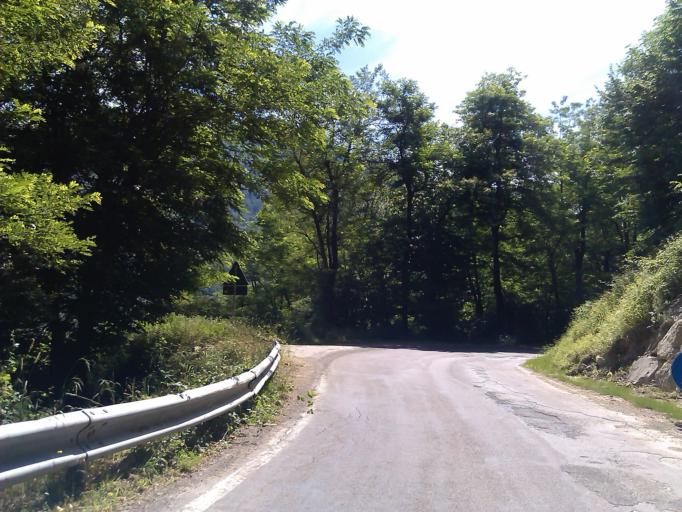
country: IT
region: Tuscany
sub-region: Provincia di Pistoia
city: Sambuca Pistoiese
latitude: 44.1027
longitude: 11.0420
